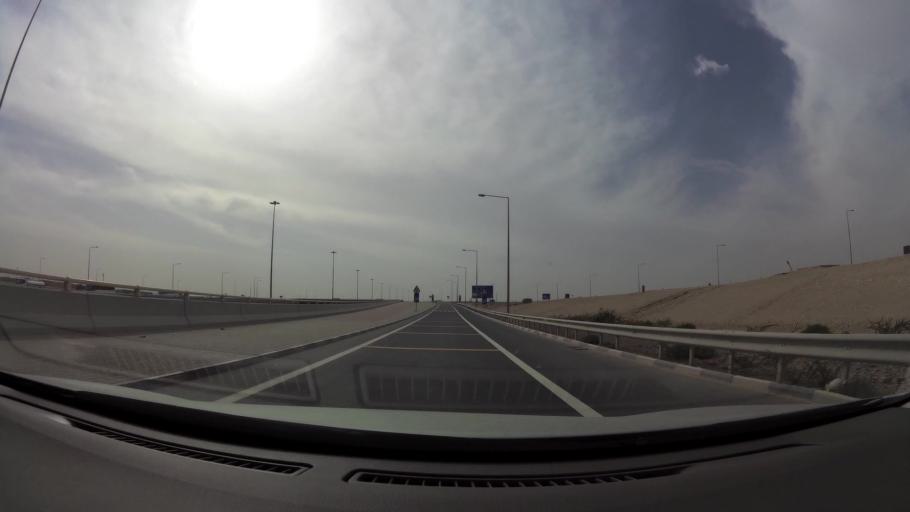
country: QA
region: Baladiyat ar Rayyan
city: Ash Shahaniyah
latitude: 25.3541
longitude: 51.2804
